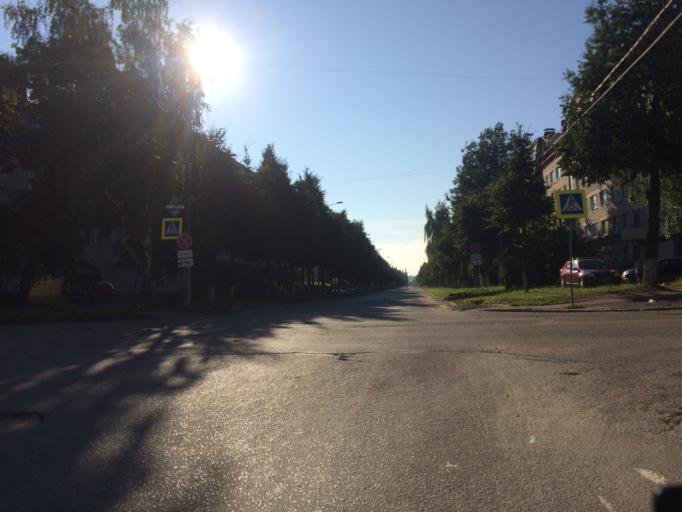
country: RU
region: Mariy-El
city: Yoshkar-Ola
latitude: 56.6407
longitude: 47.8837
